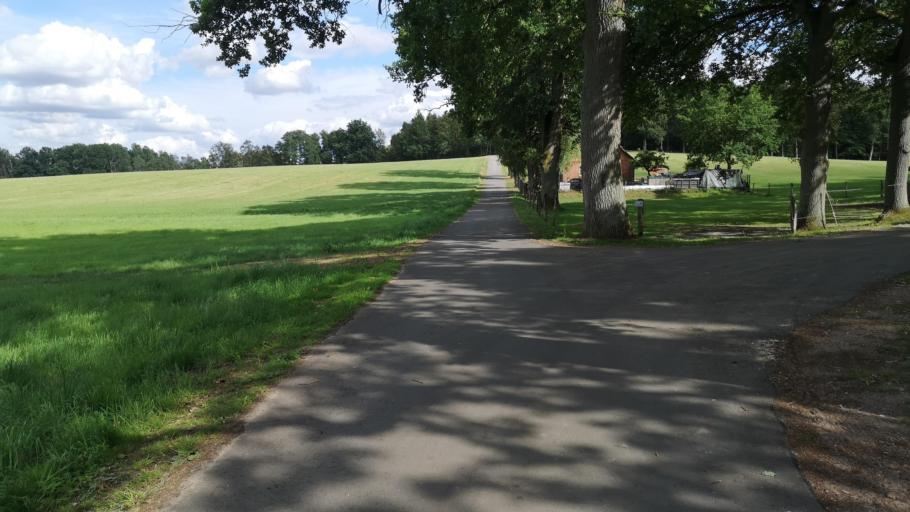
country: DE
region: Lower Saxony
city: Thomasburg
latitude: 53.2201
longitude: 10.6739
